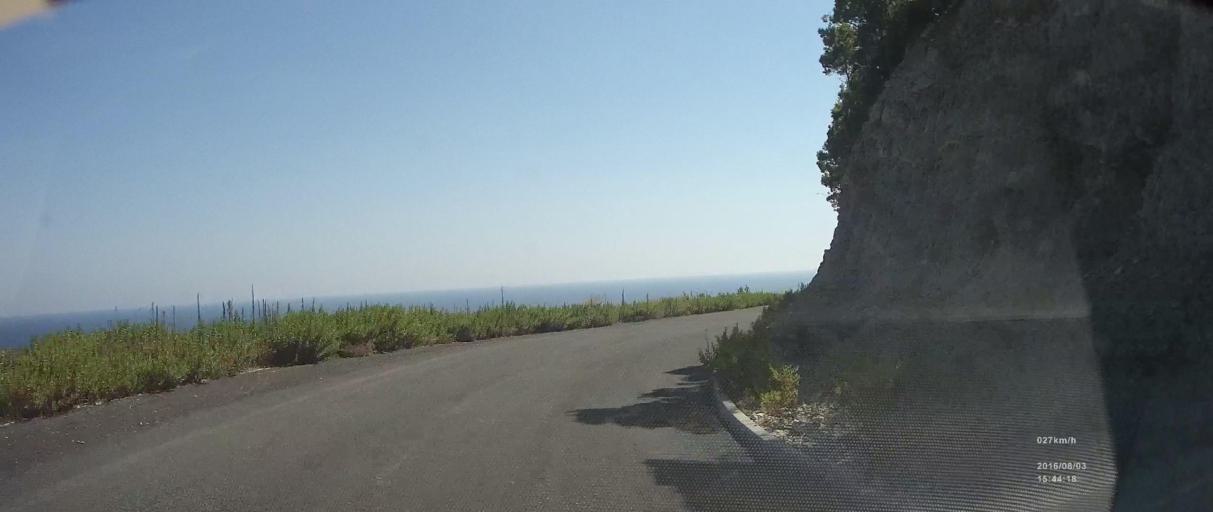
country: HR
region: Dubrovacko-Neretvanska
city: Blato
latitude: 42.7380
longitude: 17.5255
